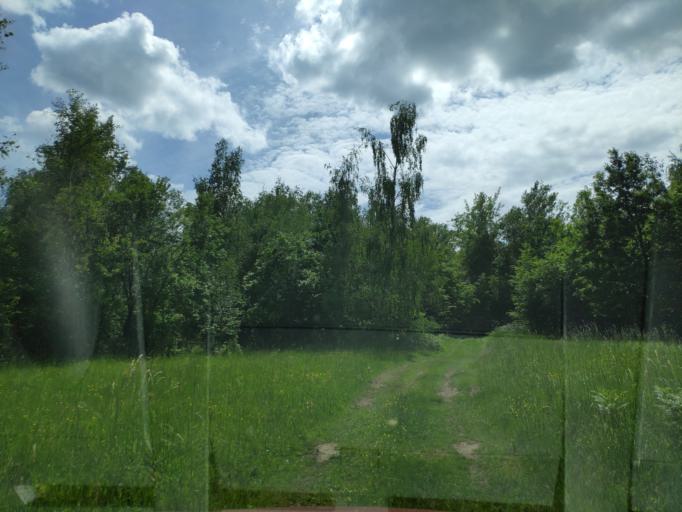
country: SK
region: Kosicky
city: Medzev
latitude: 48.7228
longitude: 20.9549
